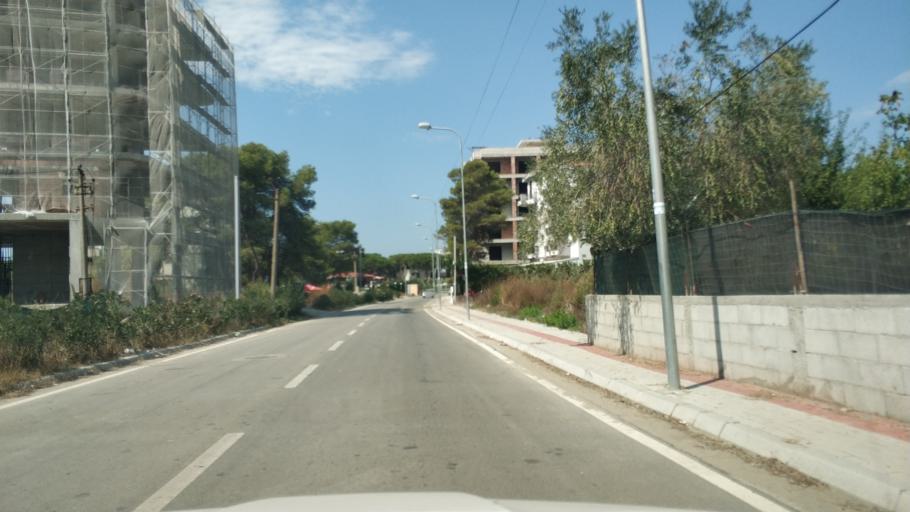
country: AL
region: Tirane
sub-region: Rrethi i Kavajes
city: Golem
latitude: 41.2373
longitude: 19.5213
